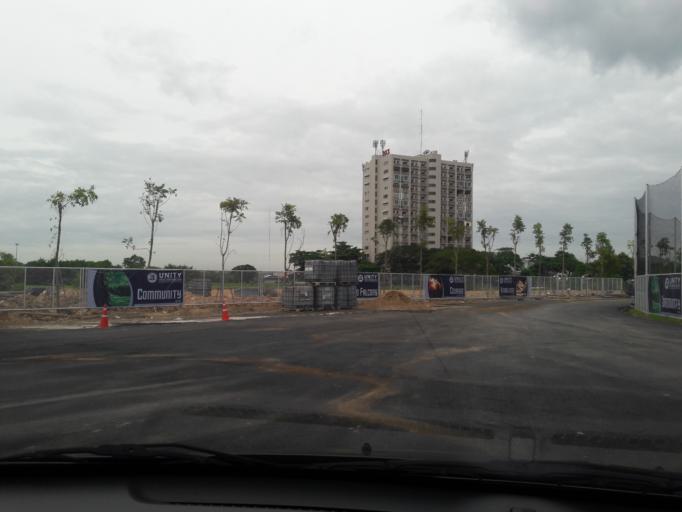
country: TH
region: Chiang Mai
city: Saraphi
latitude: 18.7489
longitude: 99.0348
